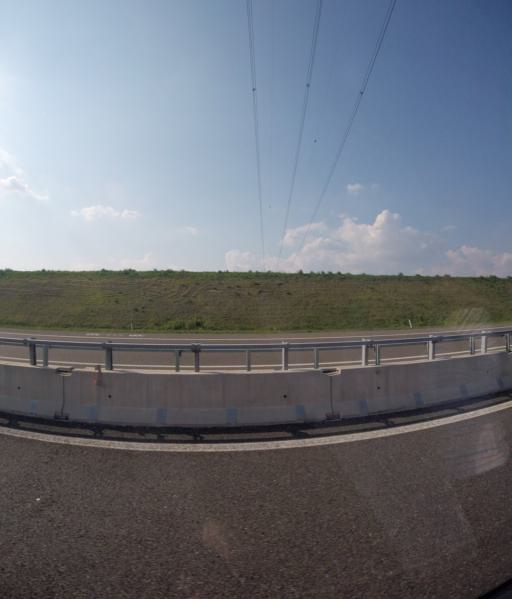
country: IT
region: Lombardy
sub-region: Provincia di Varese
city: Cislago
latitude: 45.6742
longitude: 8.9751
